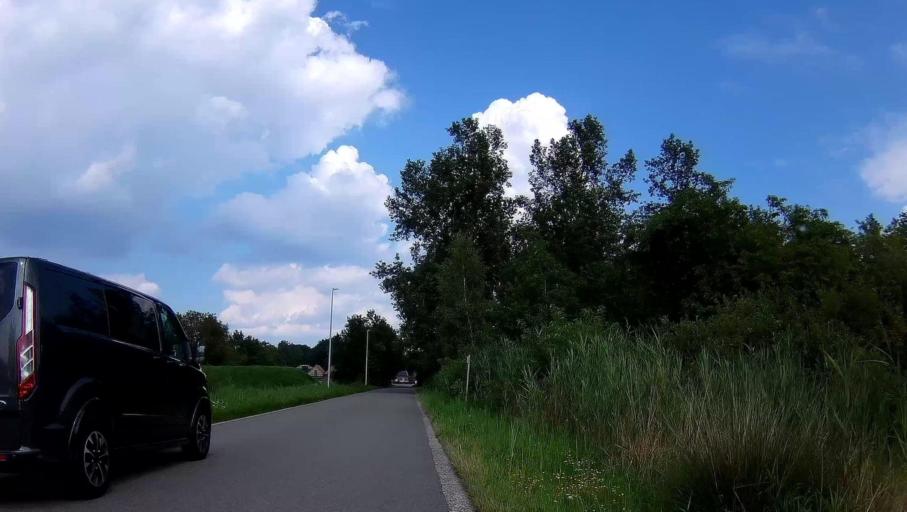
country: BE
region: Flanders
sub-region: Provincie Limburg
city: Lommel
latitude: 51.1815
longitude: 5.2721
